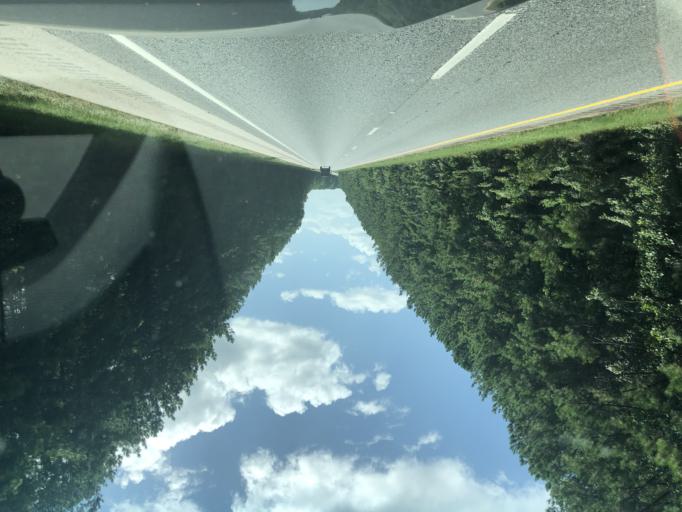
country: US
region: Georgia
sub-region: Troup County
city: La Grange
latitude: 32.9803
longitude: -84.9522
